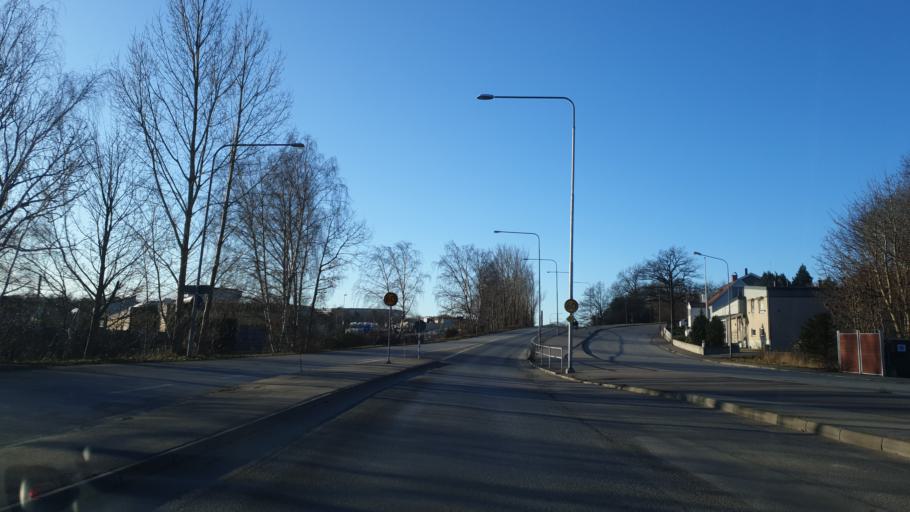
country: SE
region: Blekinge
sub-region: Karlskrona Kommun
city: Rodeby
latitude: 56.2031
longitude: 15.6291
